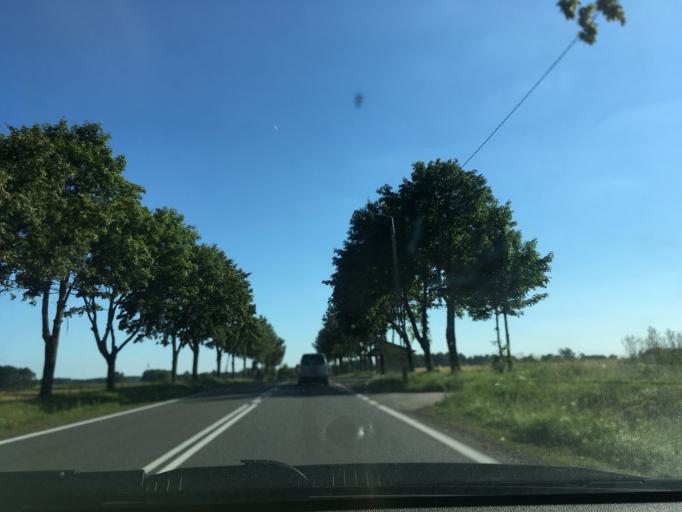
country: PL
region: Podlasie
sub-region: Powiat sokolski
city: Janow
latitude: 53.3918
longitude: 23.1137
